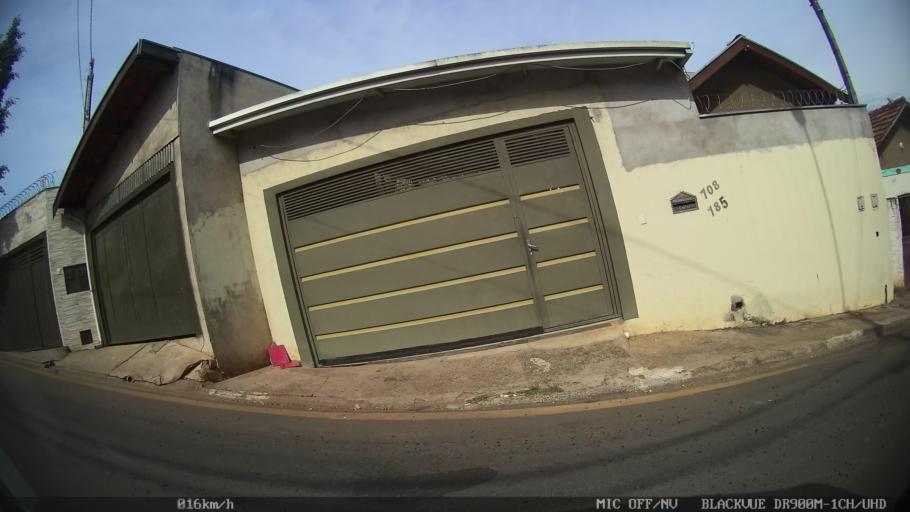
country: BR
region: Sao Paulo
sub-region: Piracicaba
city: Piracicaba
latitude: -22.7408
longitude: -47.6659
